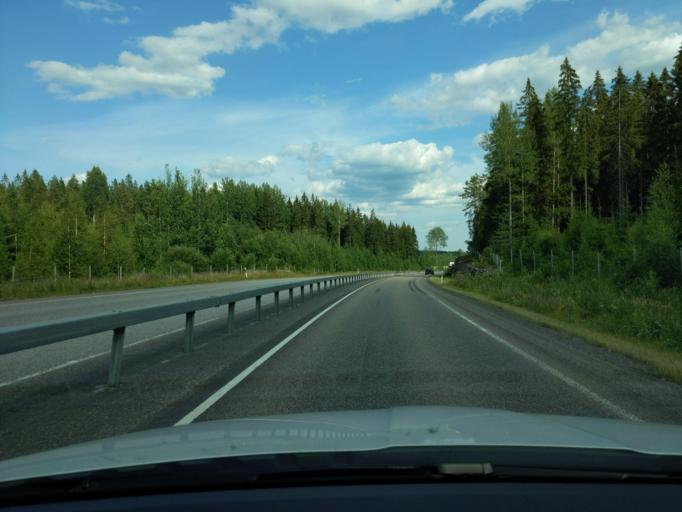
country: FI
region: Kymenlaakso
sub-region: Kouvola
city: Iitti
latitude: 60.9147
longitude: 26.2538
